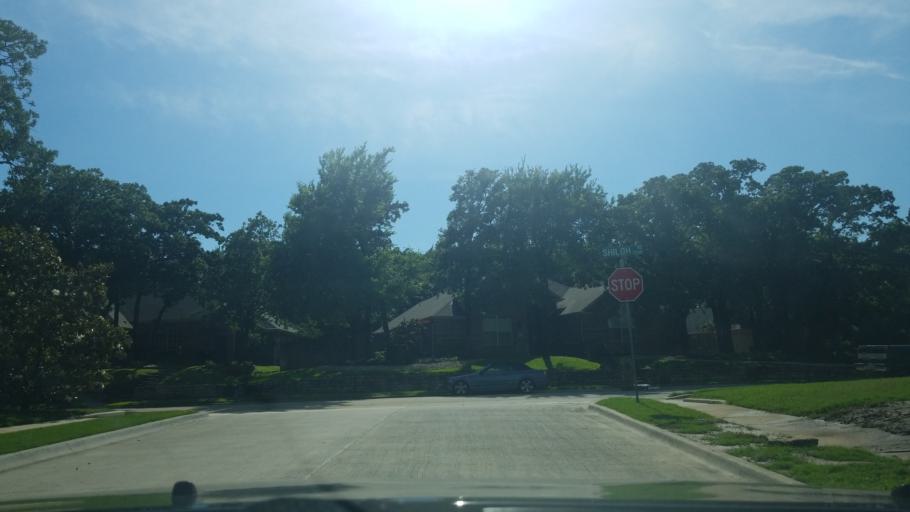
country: US
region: Texas
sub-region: Denton County
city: Denton
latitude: 33.1803
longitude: -97.1070
